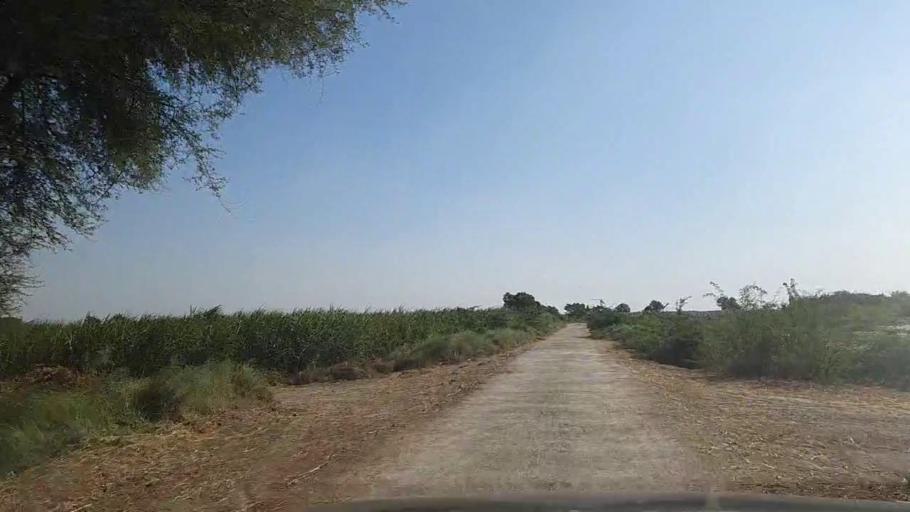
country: PK
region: Sindh
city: Daro Mehar
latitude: 24.7698
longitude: 68.0693
